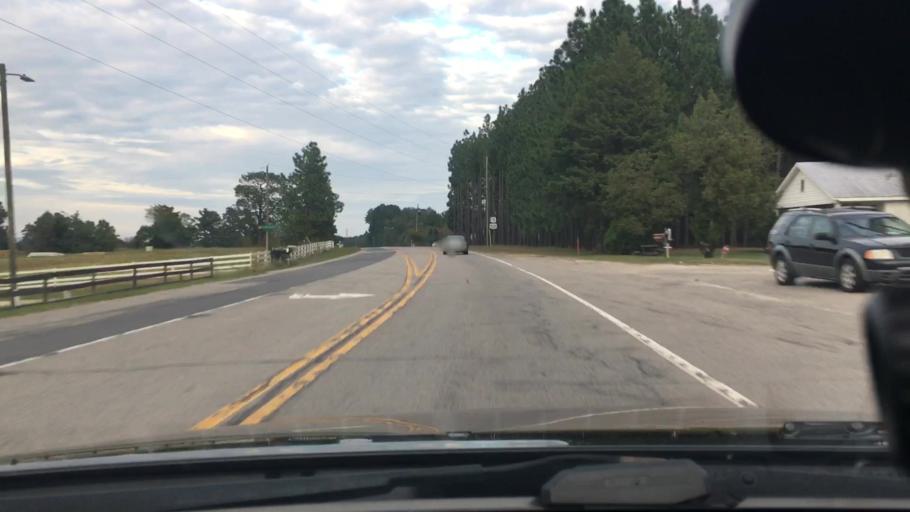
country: US
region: North Carolina
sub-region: Moore County
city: Carthage
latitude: 35.3622
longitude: -79.3204
